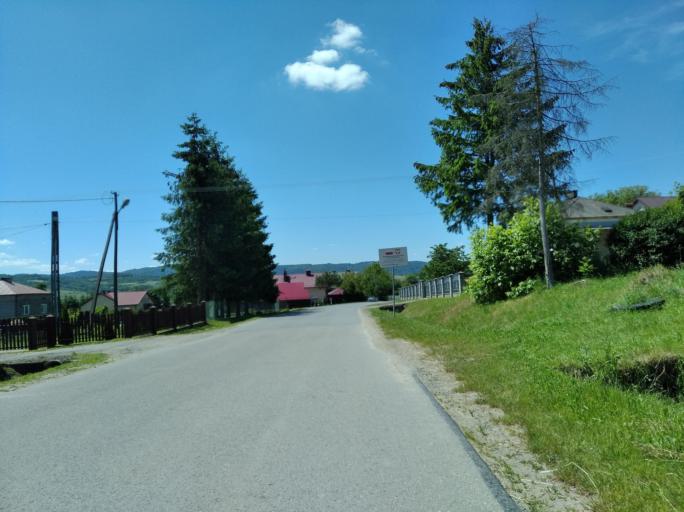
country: PL
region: Subcarpathian Voivodeship
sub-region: Powiat jasielski
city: Nowy Zmigrod
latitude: 49.6193
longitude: 21.5818
